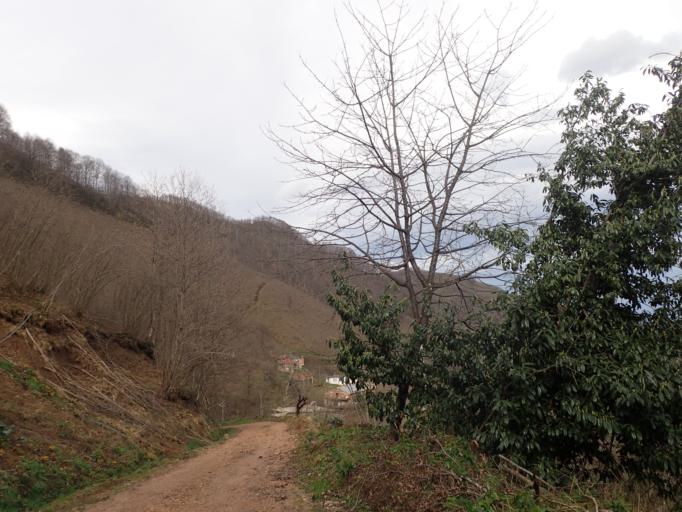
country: TR
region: Ordu
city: Camas
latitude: 40.8903
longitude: 37.5797
